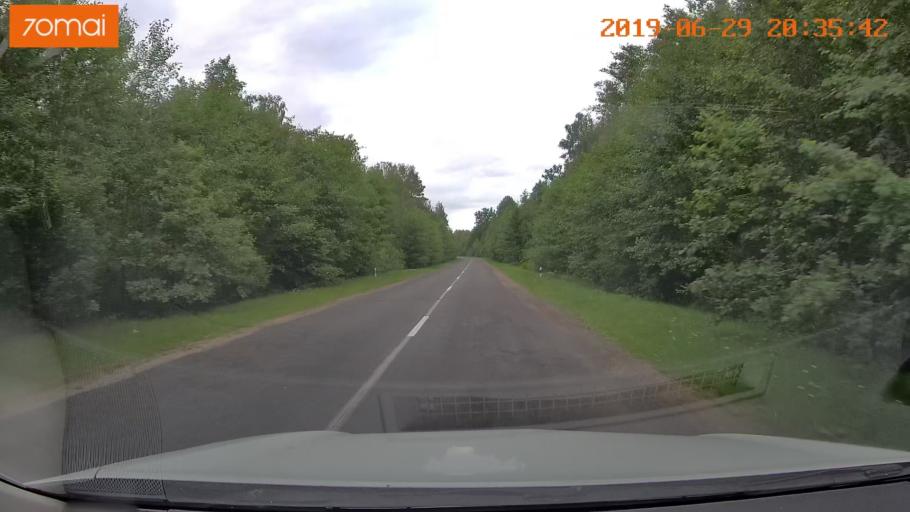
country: BY
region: Brest
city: Hantsavichy
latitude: 52.5186
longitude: 26.3526
